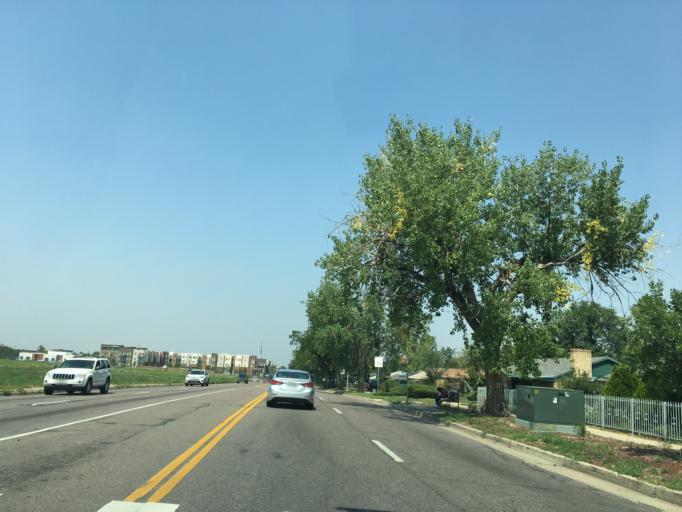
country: US
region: Colorado
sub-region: Adams County
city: Aurora
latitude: 39.7329
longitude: -104.8472
